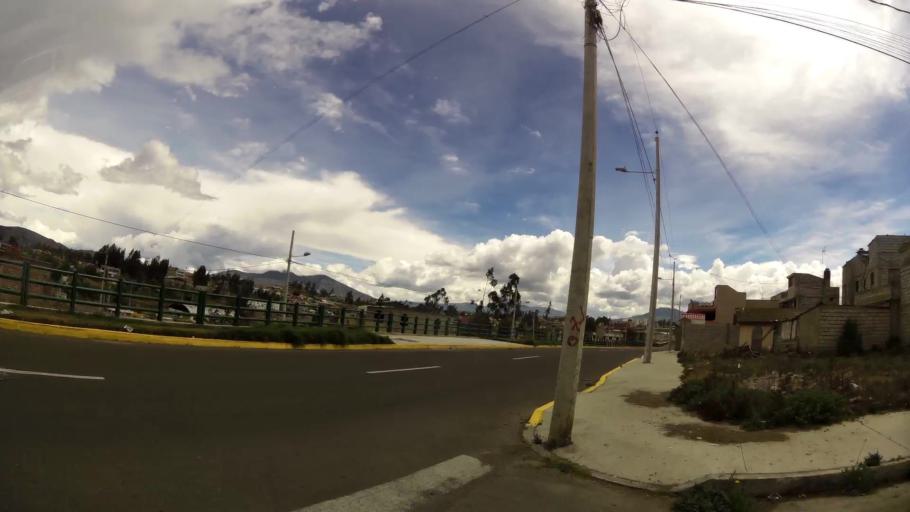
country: EC
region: Tungurahua
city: Ambato
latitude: -1.2640
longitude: -78.6078
